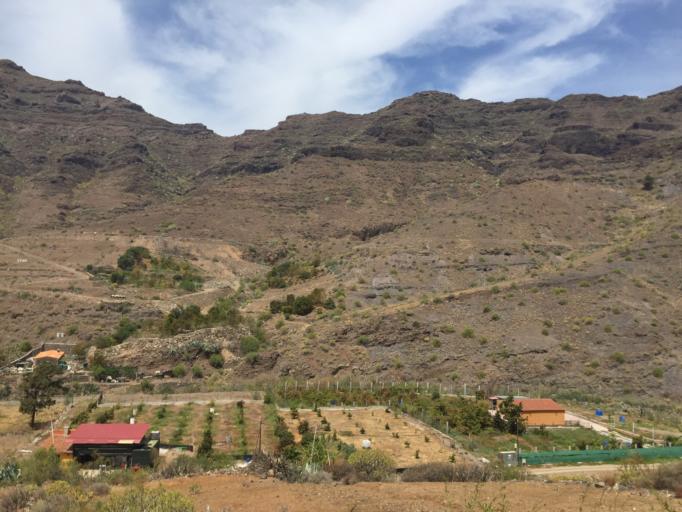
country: ES
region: Canary Islands
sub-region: Provincia de Las Palmas
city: Mogan
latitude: 27.8732
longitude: -15.7319
